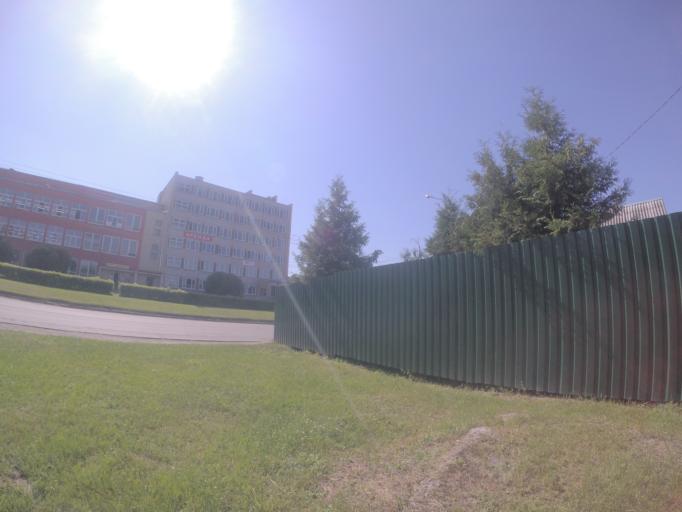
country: BY
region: Grodnenskaya
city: Hrodna
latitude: 53.6636
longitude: 23.7965
